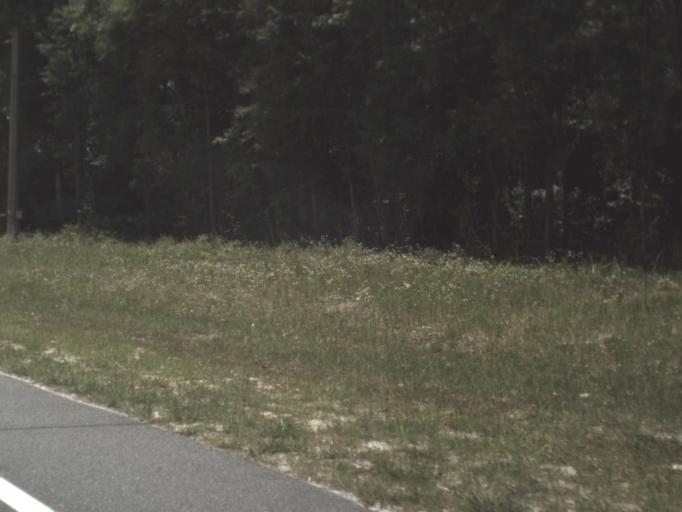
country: US
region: Florida
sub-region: Dixie County
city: Cross City
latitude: 29.7501
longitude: -82.9843
